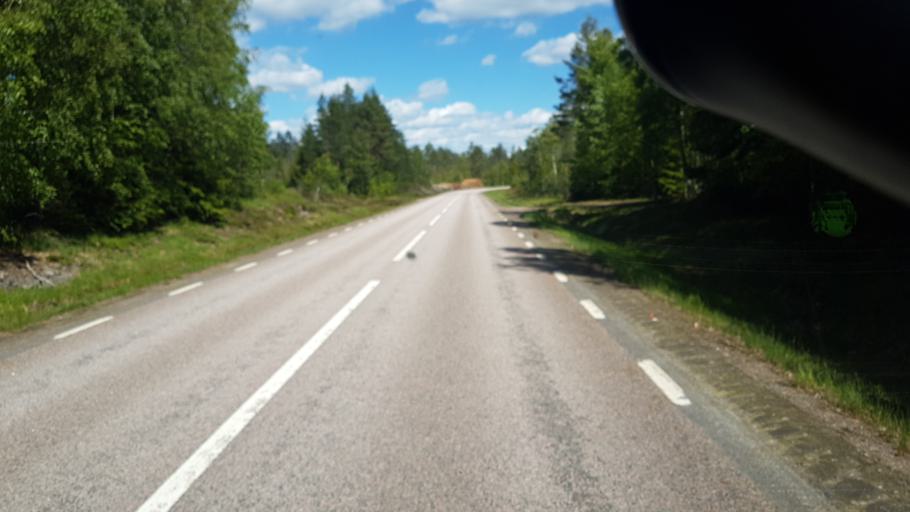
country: SE
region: Vaermland
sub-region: Sunne Kommun
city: Sunne
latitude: 59.6909
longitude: 13.0675
